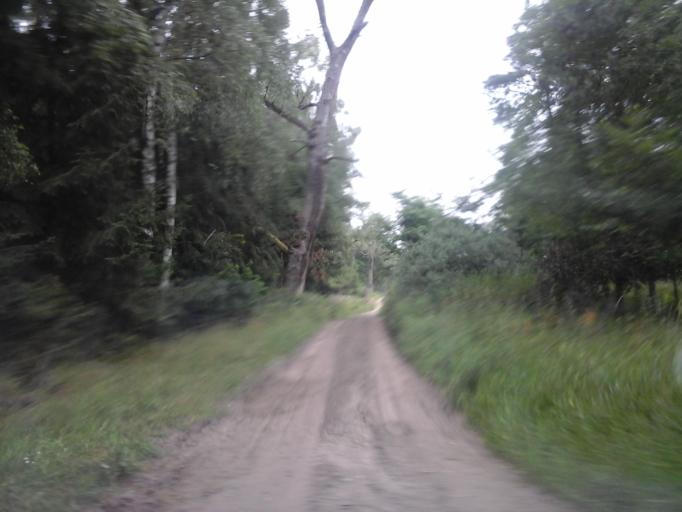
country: PL
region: West Pomeranian Voivodeship
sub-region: Powiat choszczenski
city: Recz
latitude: 53.2030
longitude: 15.5420
